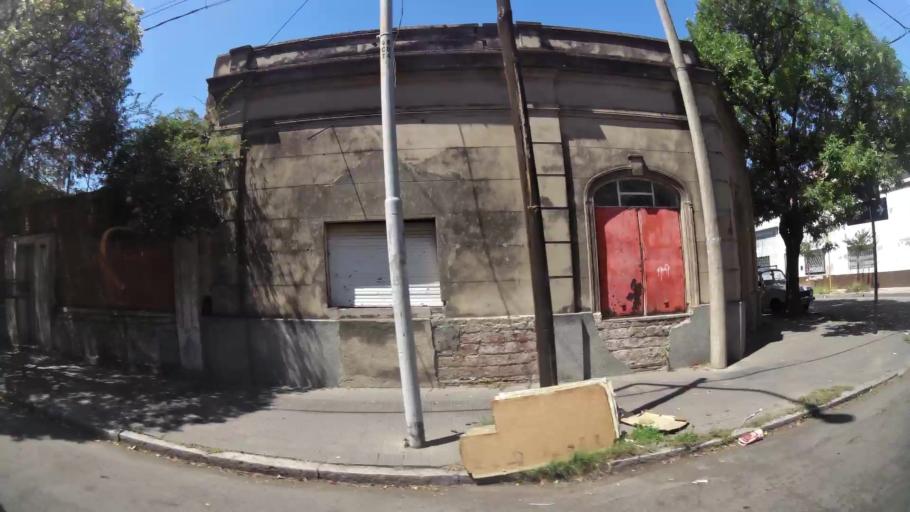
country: AR
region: Cordoba
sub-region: Departamento de Capital
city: Cordoba
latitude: -31.3874
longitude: -64.1987
